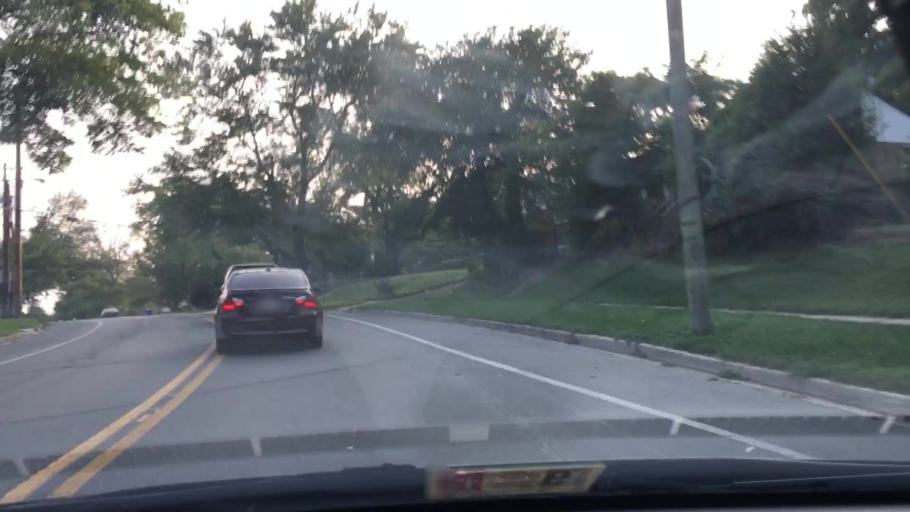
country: US
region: Maryland
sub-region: Montgomery County
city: Aspen Hill
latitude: 39.0789
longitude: -77.0903
